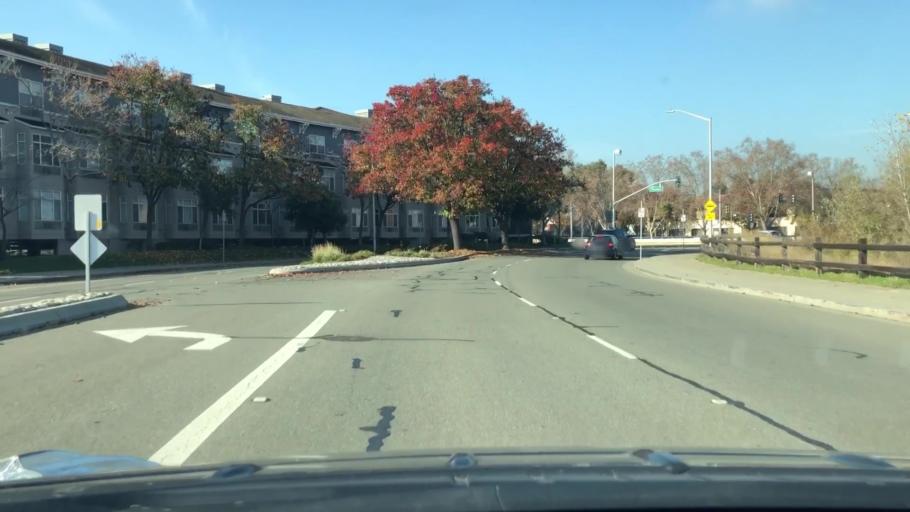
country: US
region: California
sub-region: Santa Clara County
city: Santa Clara
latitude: 37.4080
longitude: -121.9606
